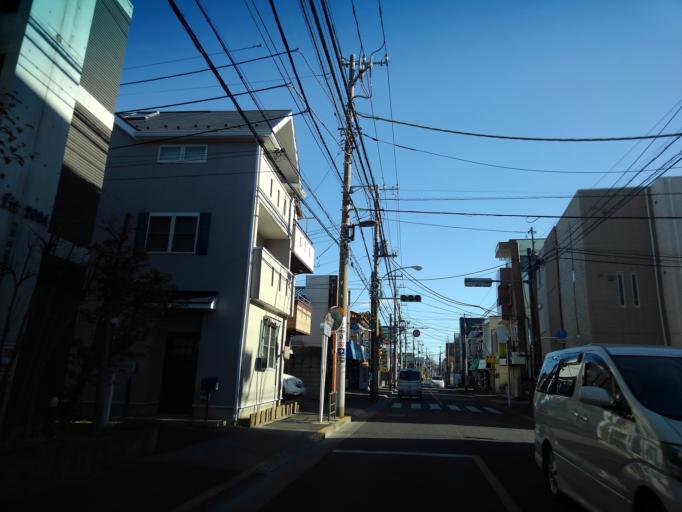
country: JP
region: Tokyo
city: Chofugaoka
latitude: 35.6608
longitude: 139.5254
